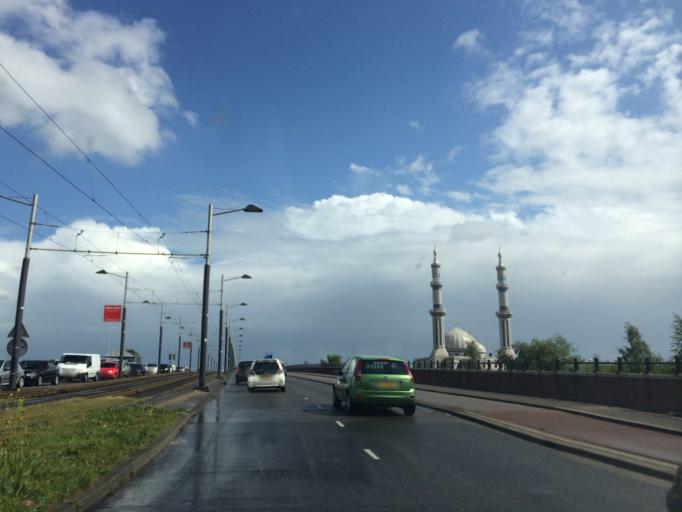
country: NL
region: South Holland
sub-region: Gemeente Rotterdam
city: Rotterdam
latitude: 51.9002
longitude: 4.5120
